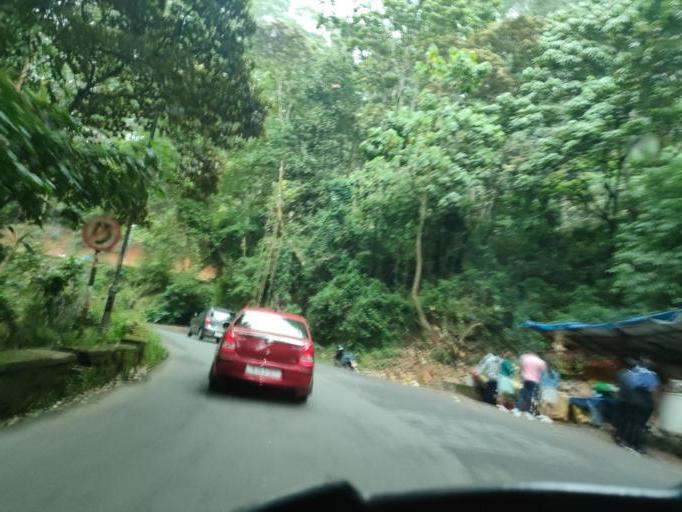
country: IN
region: Tamil Nadu
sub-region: Dindigul
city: Kodaikanal
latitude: 10.2290
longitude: 77.4994
